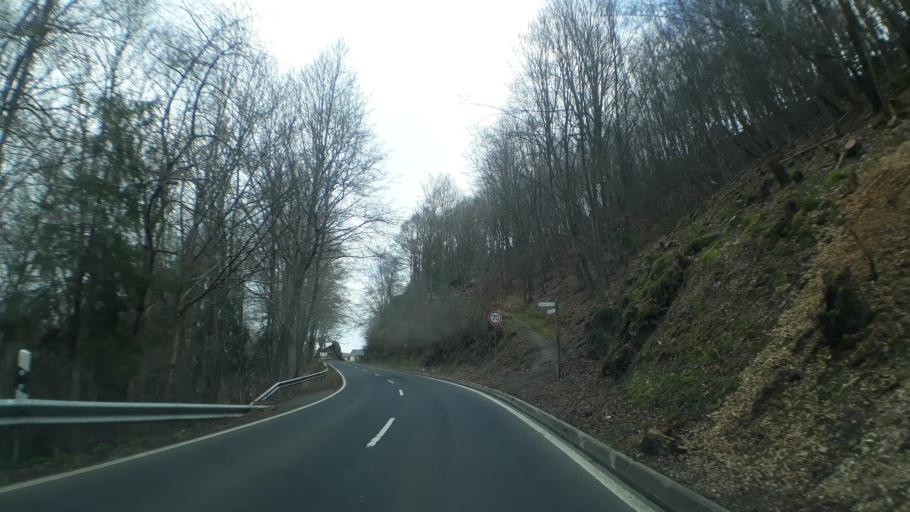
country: DE
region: North Rhine-Westphalia
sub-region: Regierungsbezirk Koln
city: Simmerath
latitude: 50.5809
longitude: 6.3492
